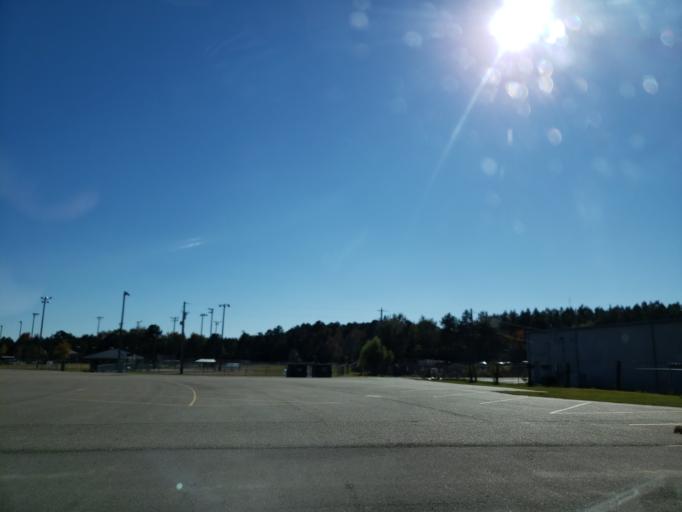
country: US
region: Mississippi
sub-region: Lamar County
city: West Hattiesburg
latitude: 31.3169
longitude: -89.4029
